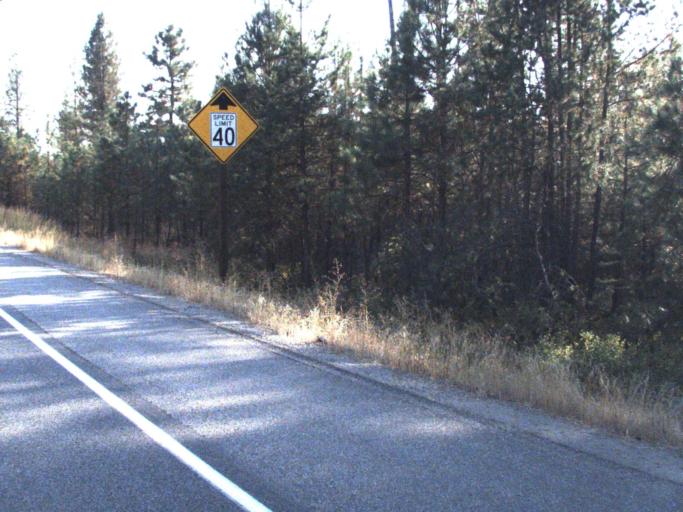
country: US
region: Washington
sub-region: Spokane County
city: Deer Park
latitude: 47.9799
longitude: -117.3496
